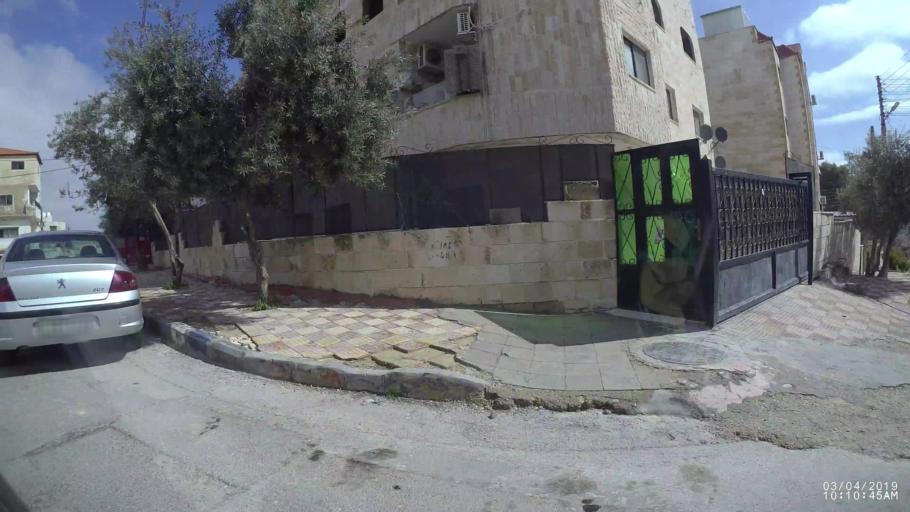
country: JO
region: Amman
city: Wadi as Sir
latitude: 31.9498
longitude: 35.8297
